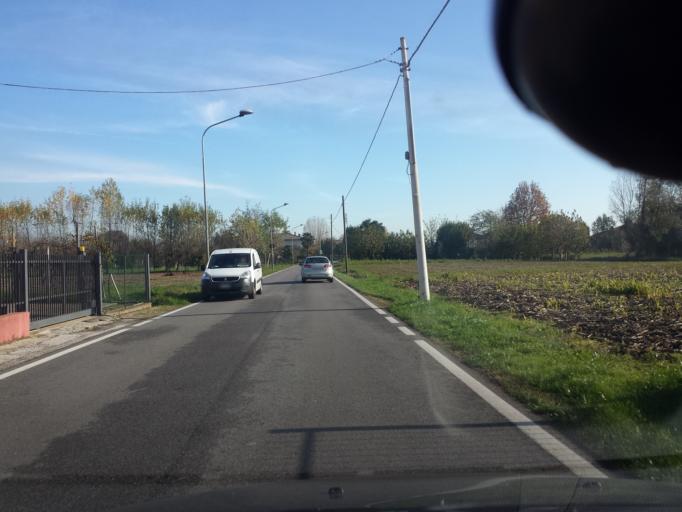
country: IT
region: Veneto
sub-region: Provincia di Vicenza
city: Caldogno-Rettorgole-Cresole
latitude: 45.6110
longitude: 11.5175
